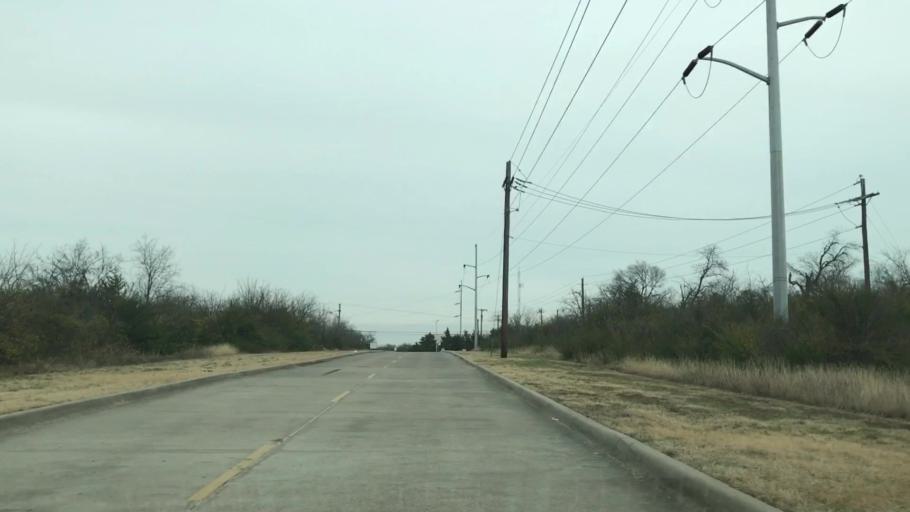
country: US
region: Texas
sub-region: Dallas County
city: Cockrell Hill
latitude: 32.7476
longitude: -96.8960
